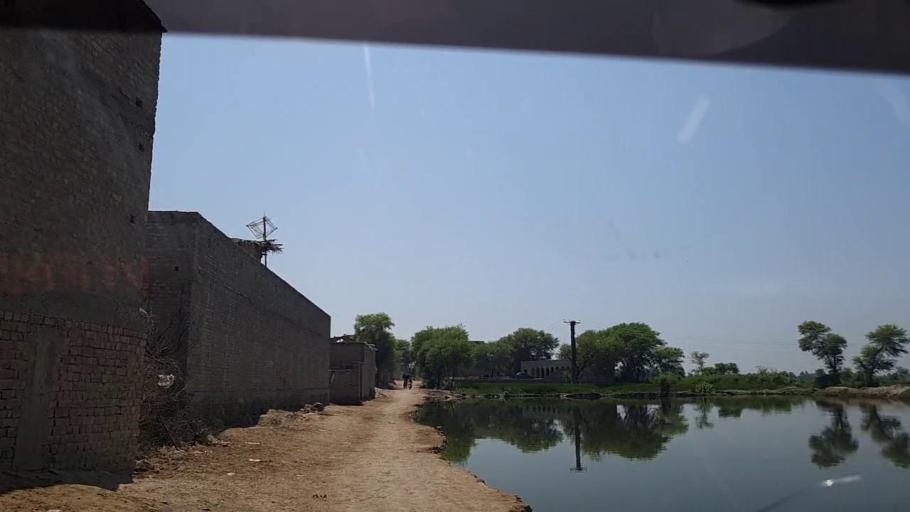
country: PK
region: Sindh
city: Ghauspur
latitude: 28.1661
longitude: 69.1259
